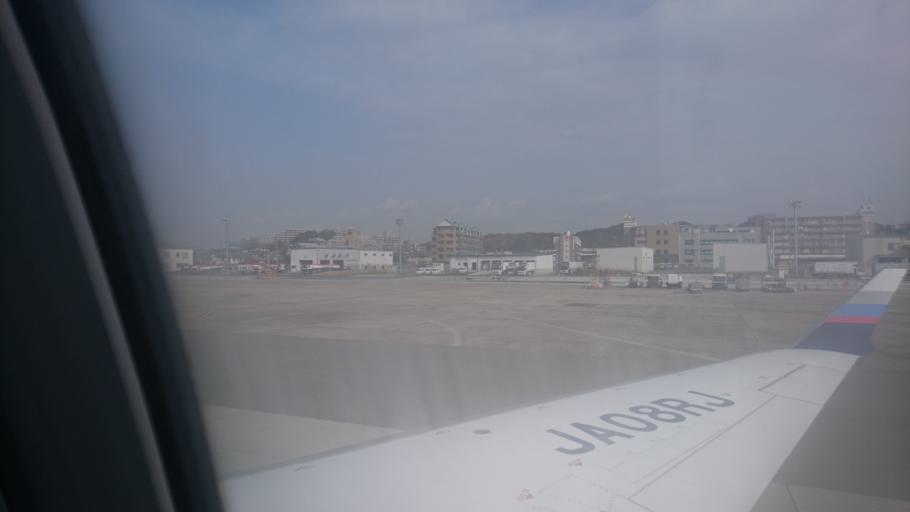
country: JP
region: Fukuoka
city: Fukuoka-shi
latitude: 33.5871
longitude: 130.4522
